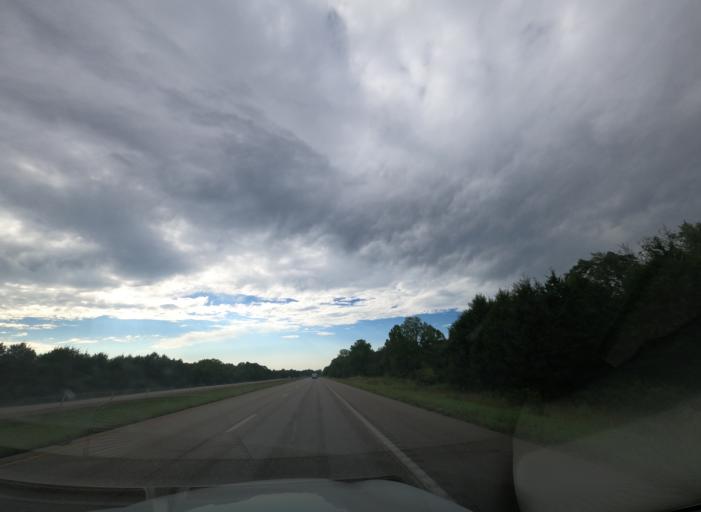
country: US
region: Missouri
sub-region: Sainte Genevieve County
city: Sainte Genevieve
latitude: 37.9662
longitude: -90.1791
